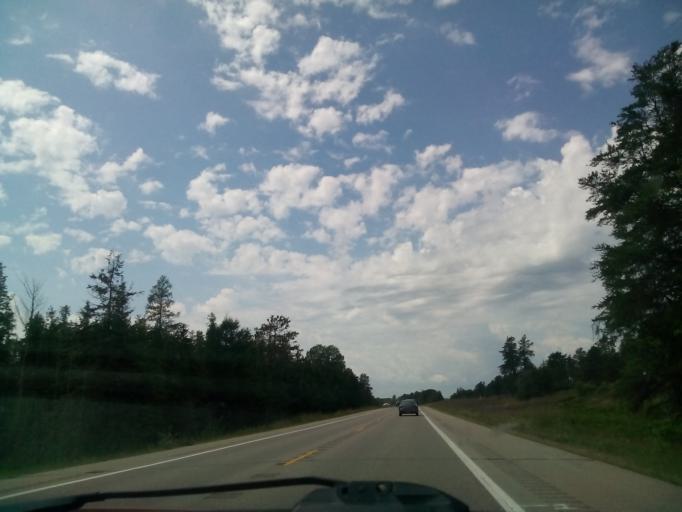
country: US
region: Michigan
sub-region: Delta County
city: Gladstone
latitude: 45.8942
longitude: -86.6910
